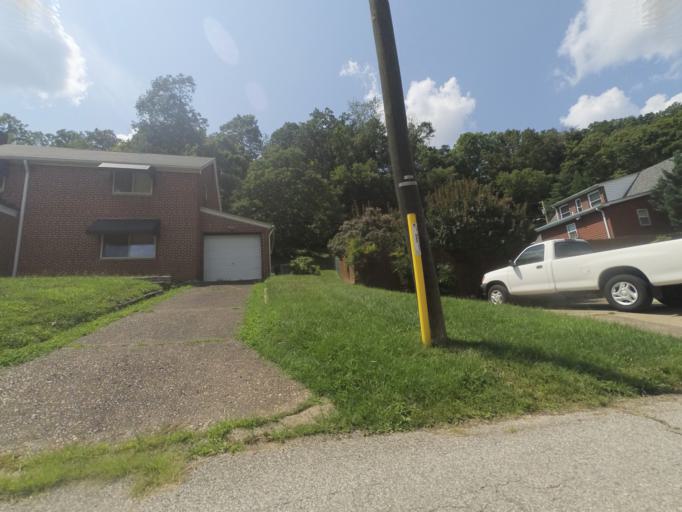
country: US
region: West Virginia
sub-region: Cabell County
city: Huntington
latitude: 38.3983
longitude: -82.4284
